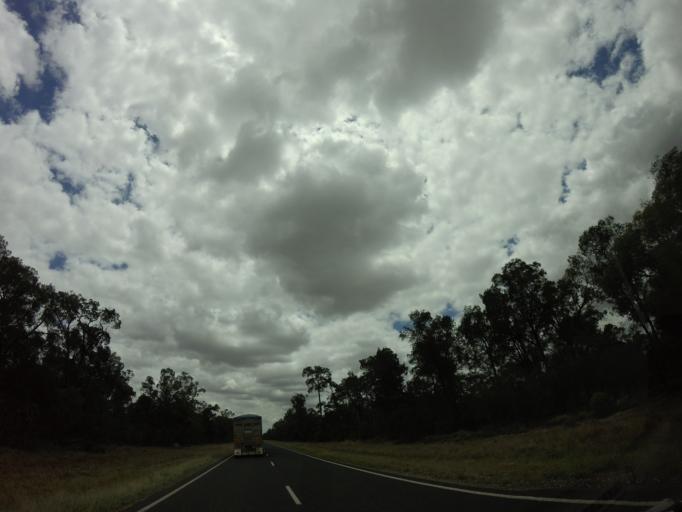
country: AU
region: Queensland
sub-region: Goondiwindi
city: Goondiwindi
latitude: -28.4246
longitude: 150.3030
